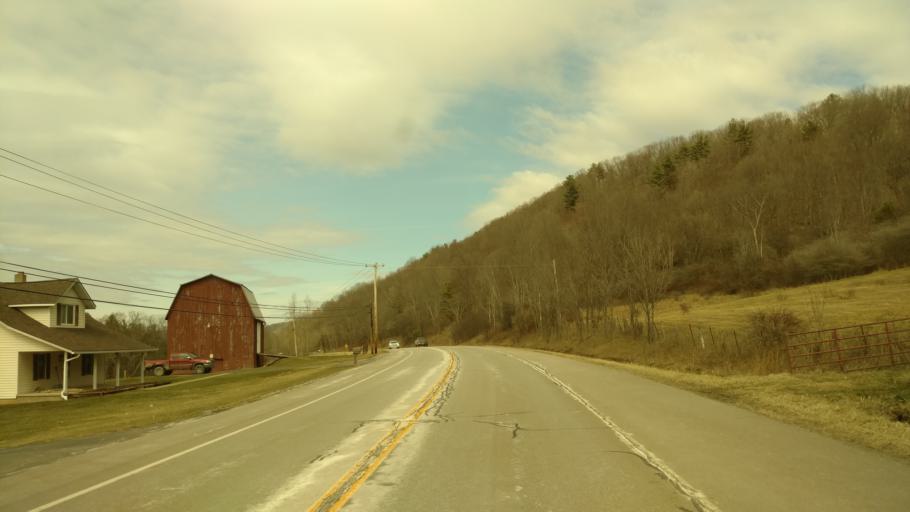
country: US
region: New York
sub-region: Allegany County
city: Wellsville
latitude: 42.0682
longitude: -77.9191
